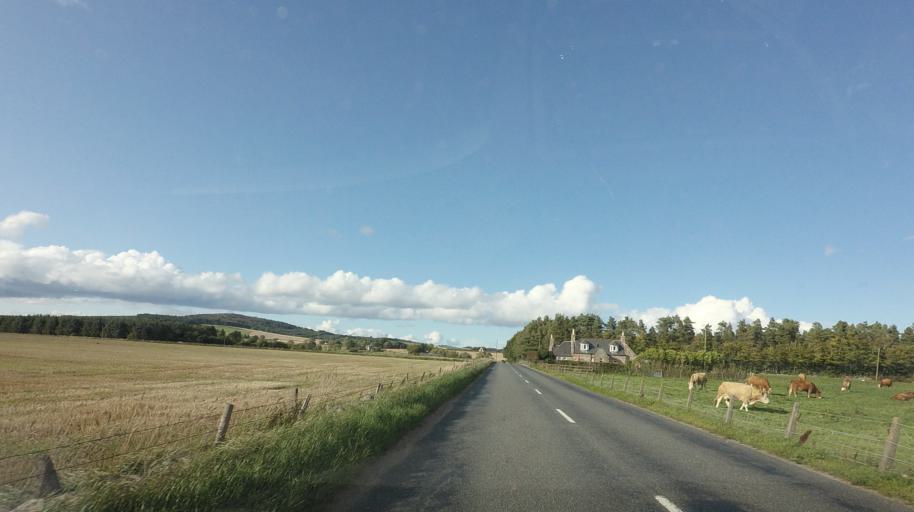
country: GB
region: Scotland
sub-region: Aberdeenshire
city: Banchory
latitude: 57.1293
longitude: -2.4276
